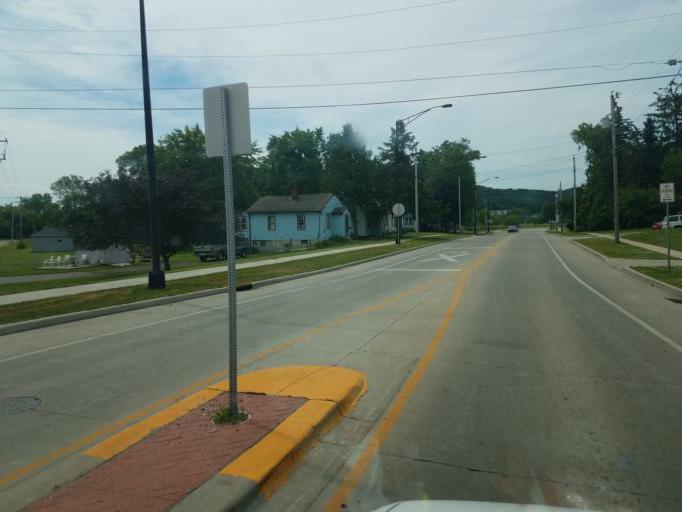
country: US
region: Wisconsin
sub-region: Juneau County
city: Mauston
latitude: 43.7924
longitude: -90.0733
